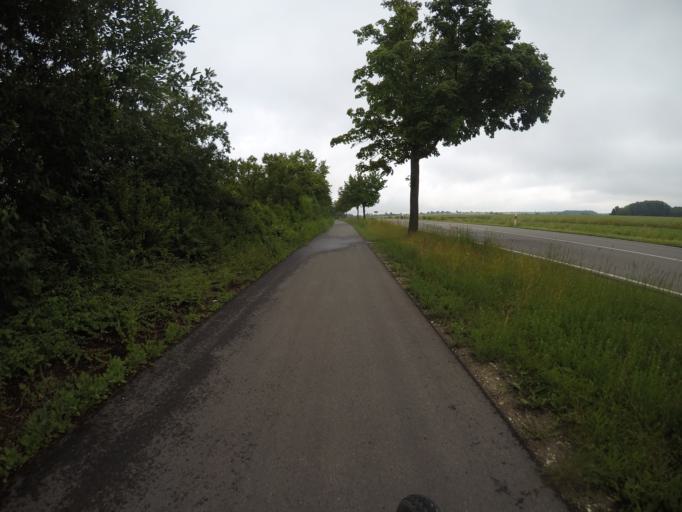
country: DE
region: Baden-Wuerttemberg
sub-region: Tuebingen Region
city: Ulm
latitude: 48.4308
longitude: 9.9855
